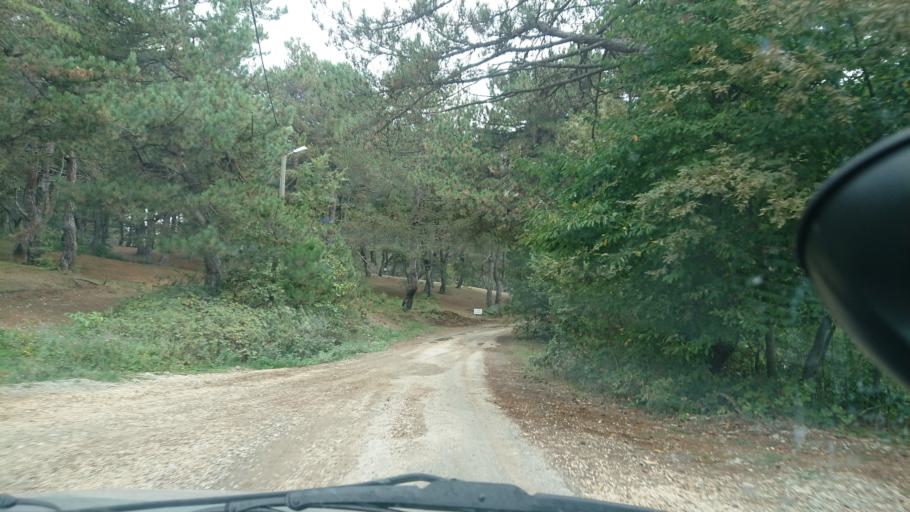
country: TR
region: Bilecik
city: Pazaryeri
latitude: 40.0121
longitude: 29.7978
